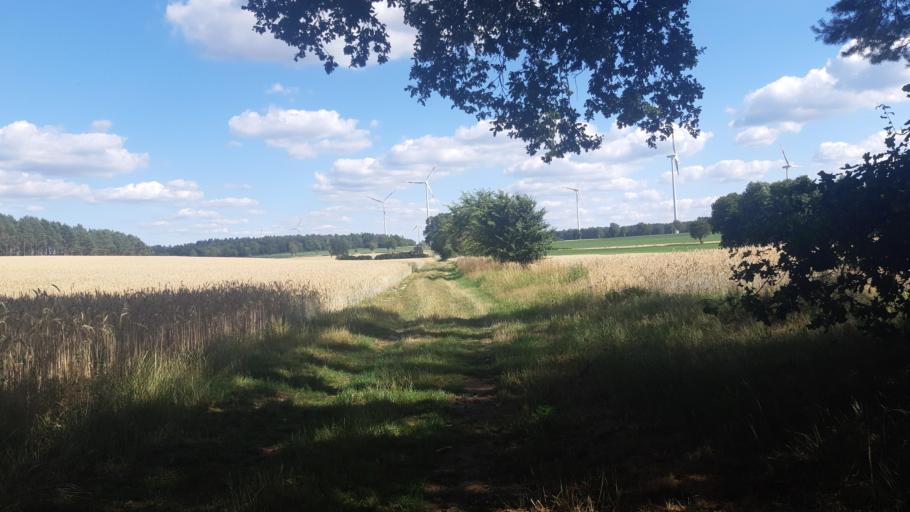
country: DE
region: Lower Saxony
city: Dahlem
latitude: 53.1973
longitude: 10.7674
